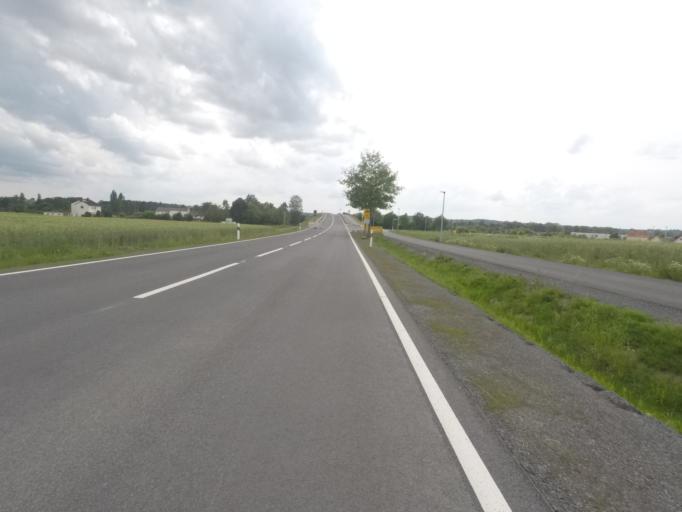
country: DE
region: North Rhine-Westphalia
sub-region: Regierungsbezirk Detmold
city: Rodinghausen
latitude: 52.1994
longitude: 8.4818
